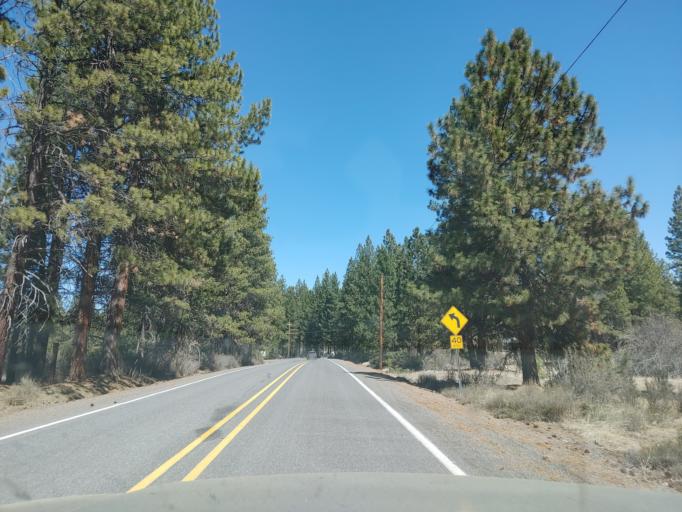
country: US
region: Oregon
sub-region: Klamath County
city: Klamath Falls
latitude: 42.5484
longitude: -121.8979
